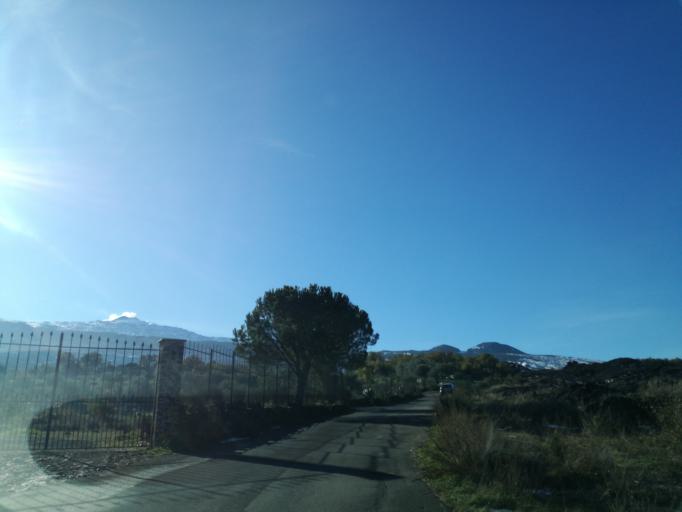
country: IT
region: Sicily
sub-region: Catania
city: Randazzo
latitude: 37.8650
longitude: 14.9802
